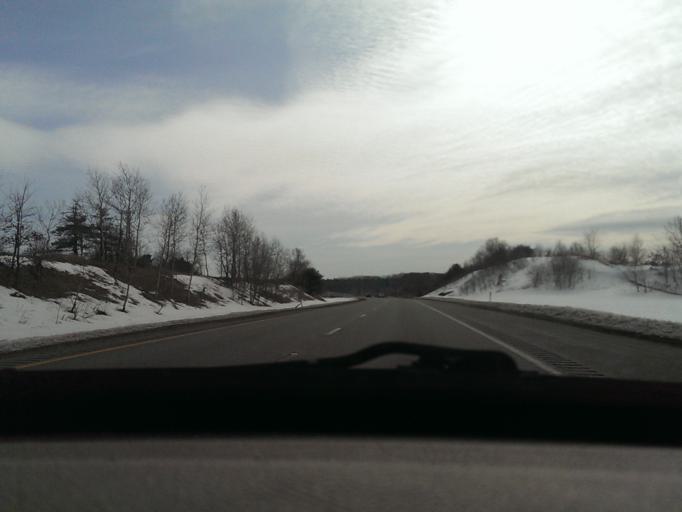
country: US
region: Massachusetts
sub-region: Worcester County
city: East Douglas
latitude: 42.1072
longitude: -71.7055
